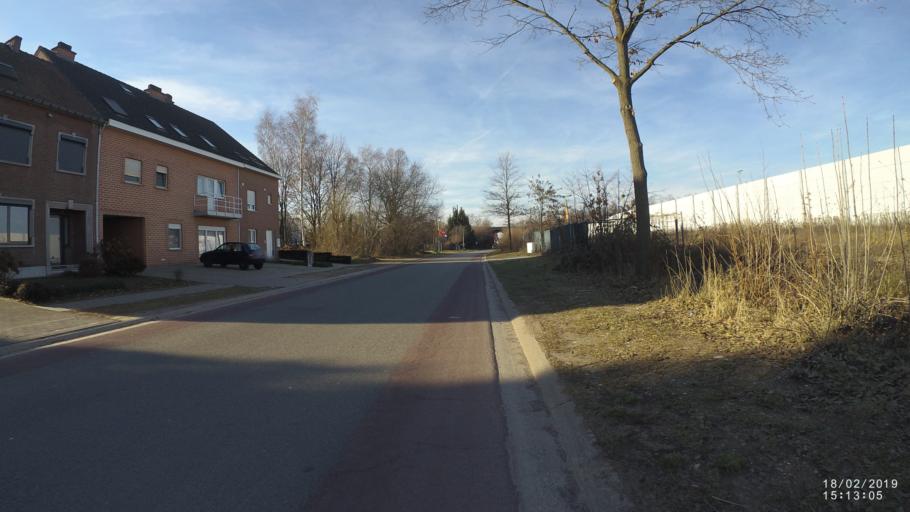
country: BE
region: Flanders
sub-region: Provincie Limburg
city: Hasselt
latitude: 50.9393
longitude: 5.3139
